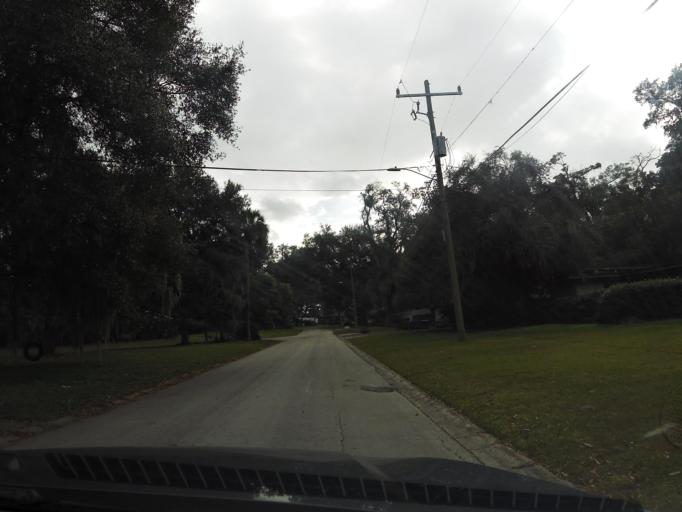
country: US
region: Florida
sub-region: Duval County
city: Jacksonville
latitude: 30.3242
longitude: -81.5914
